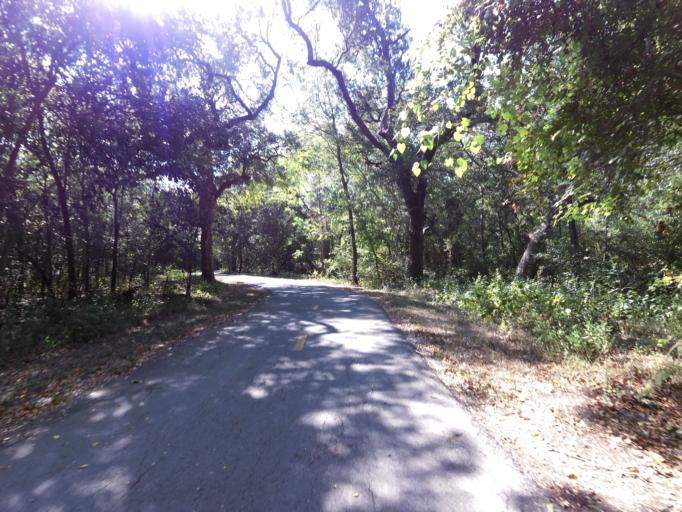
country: US
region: Texas
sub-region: Bexar County
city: Kirby
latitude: 29.4462
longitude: -98.4214
